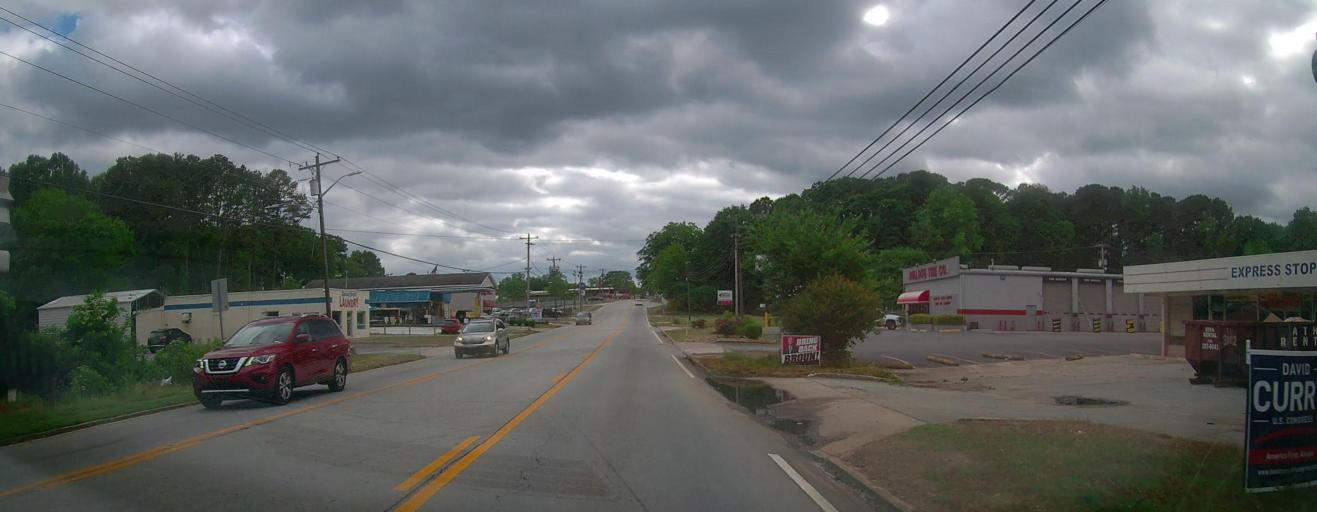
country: US
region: Georgia
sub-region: Walton County
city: Monroe
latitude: 33.7984
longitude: -83.7047
